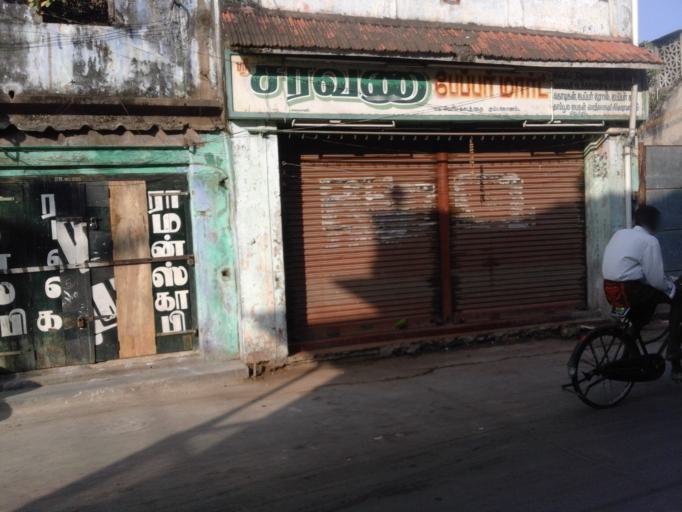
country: IN
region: Tamil Nadu
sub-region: Thanjavur
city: Kumbakonam
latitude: 10.9610
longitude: 79.3730
